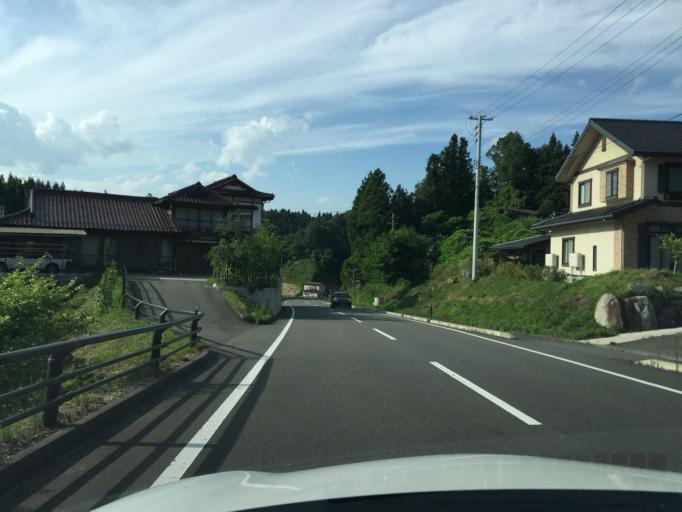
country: JP
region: Fukushima
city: Miharu
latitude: 37.3822
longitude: 140.5073
